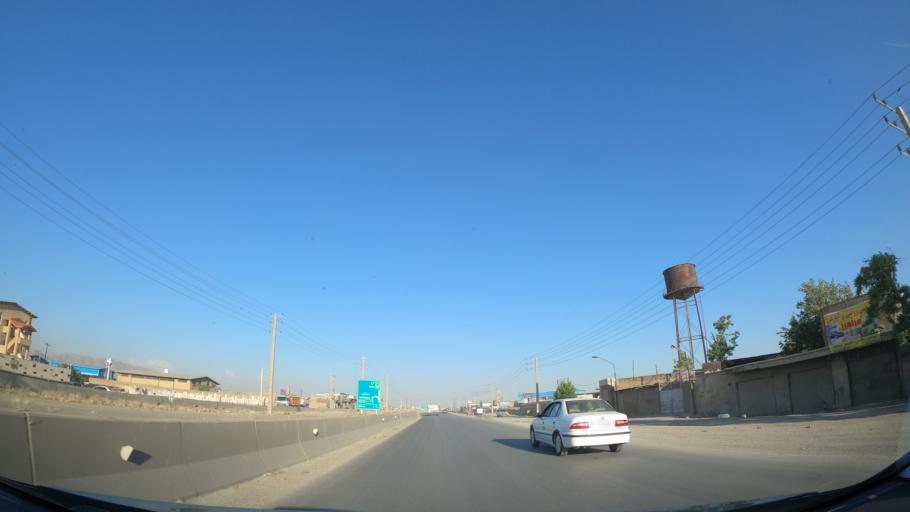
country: IR
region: Alborz
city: Hashtgerd
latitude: 35.9158
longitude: 50.7570
